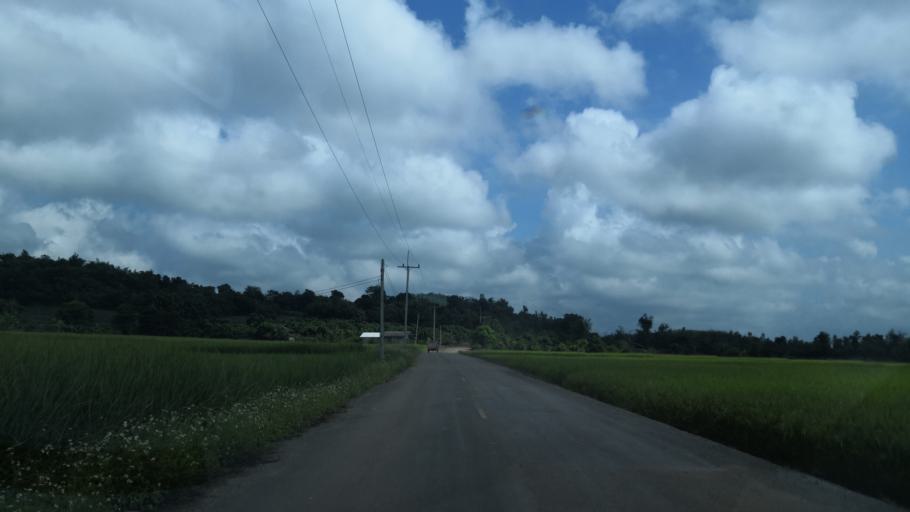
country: TH
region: Chiang Rai
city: Wiang Chiang Rung
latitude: 20.0183
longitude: 100.0414
